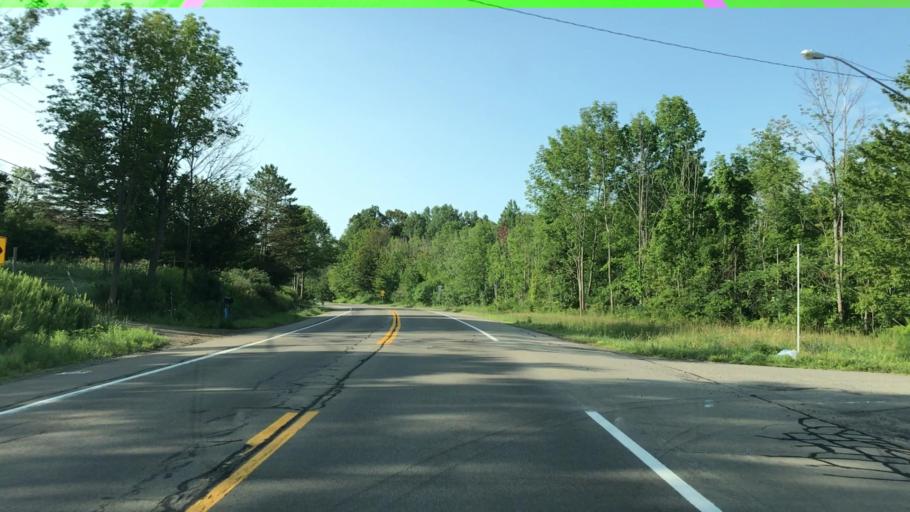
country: US
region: New York
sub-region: Chautauqua County
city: Fredonia
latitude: 42.3738
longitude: -79.3143
